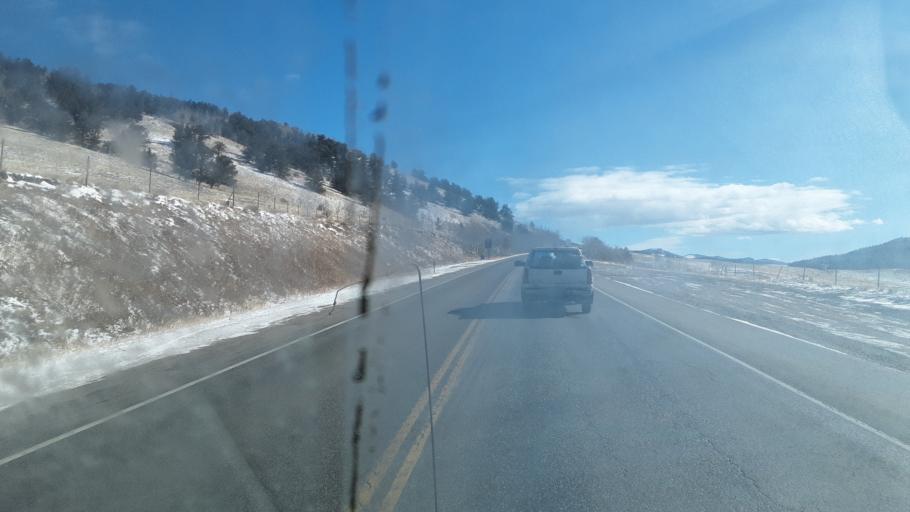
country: US
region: Colorado
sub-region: Summit County
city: Breckenridge
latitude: 39.4040
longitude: -105.7680
